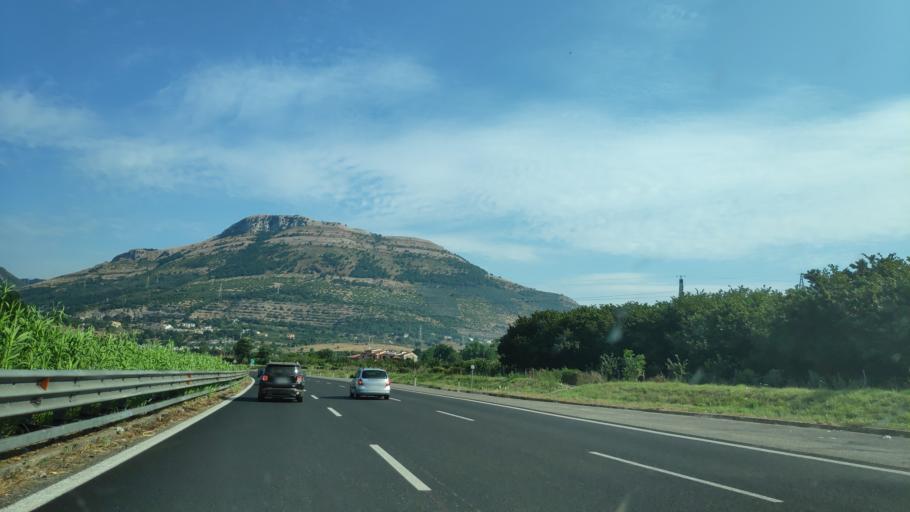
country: IT
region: Campania
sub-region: Provincia di Salerno
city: Pezzano-Filetta
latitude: 40.6793
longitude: 14.8574
